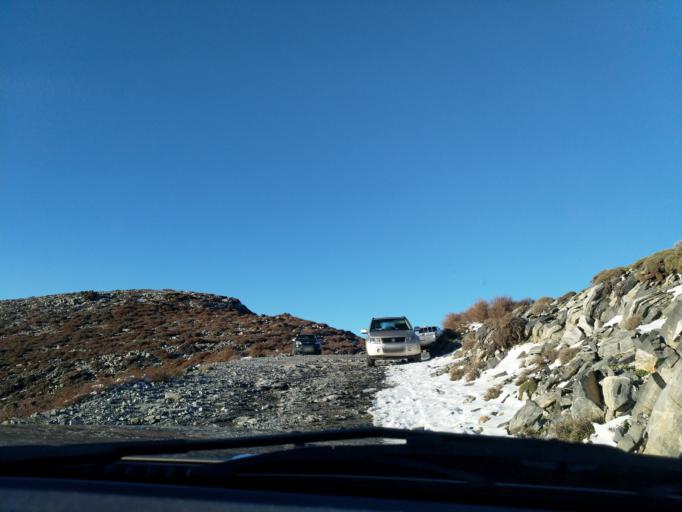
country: GR
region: Crete
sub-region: Nomos Chanias
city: Perivolia
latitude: 35.3215
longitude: 23.9295
